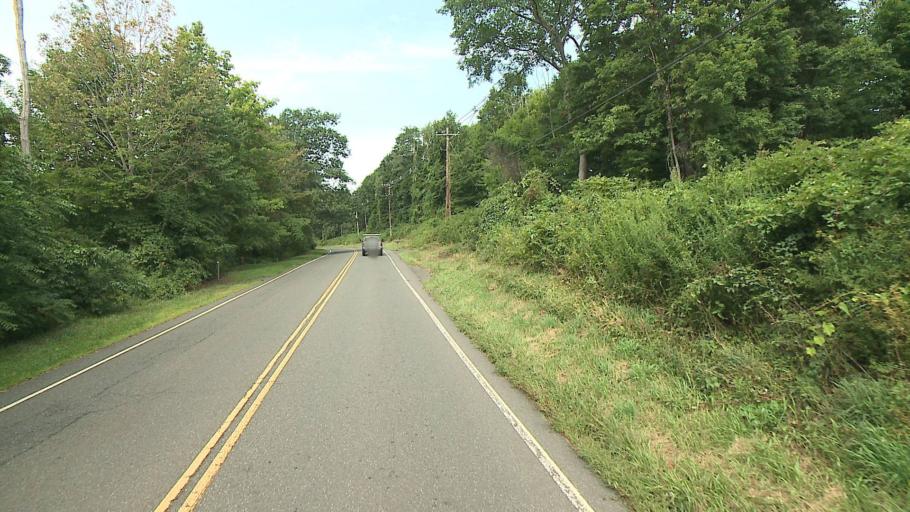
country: US
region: Connecticut
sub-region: Litchfield County
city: Bethlehem Village
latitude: 41.6035
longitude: -73.2414
